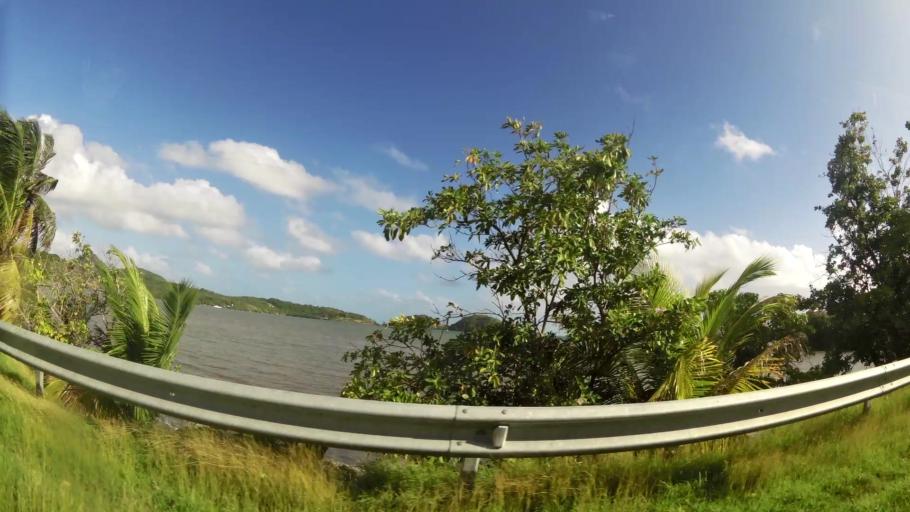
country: MQ
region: Martinique
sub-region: Martinique
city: Le Francois
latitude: 14.6195
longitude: -60.8946
